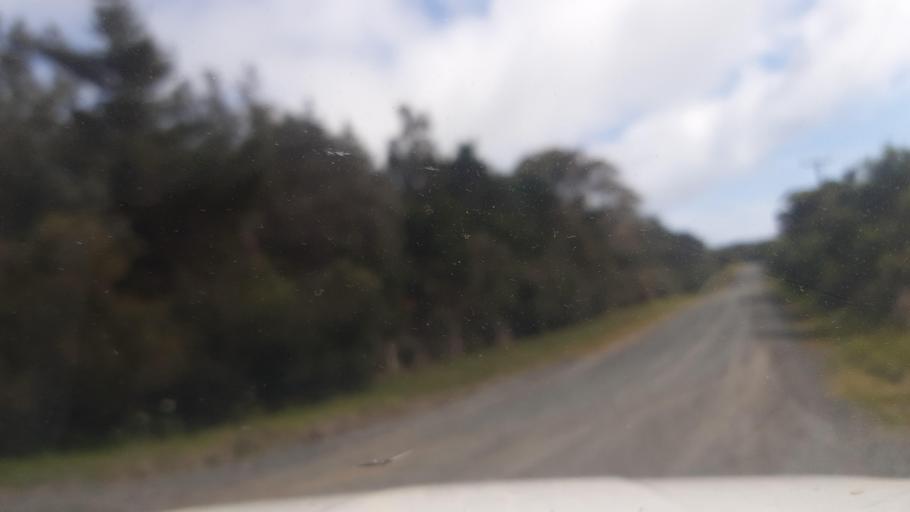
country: NZ
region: Northland
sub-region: Far North District
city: Kaitaia
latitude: -34.7420
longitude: 173.1121
